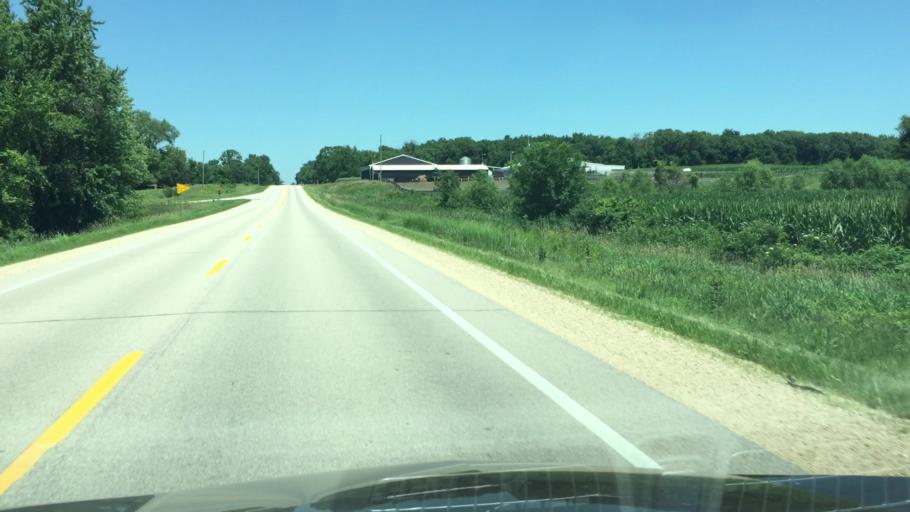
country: US
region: Iowa
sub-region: Cedar County
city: Mechanicsville
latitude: 42.0215
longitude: -91.1367
